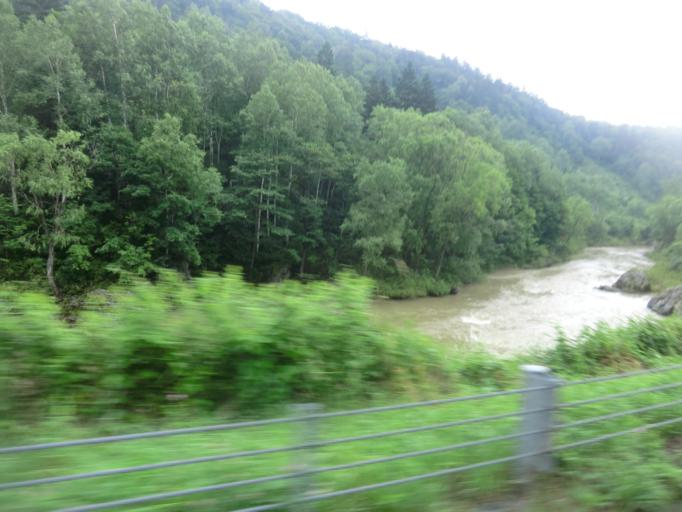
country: JP
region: Hokkaido
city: Nayoro
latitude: 44.1087
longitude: 142.1392
